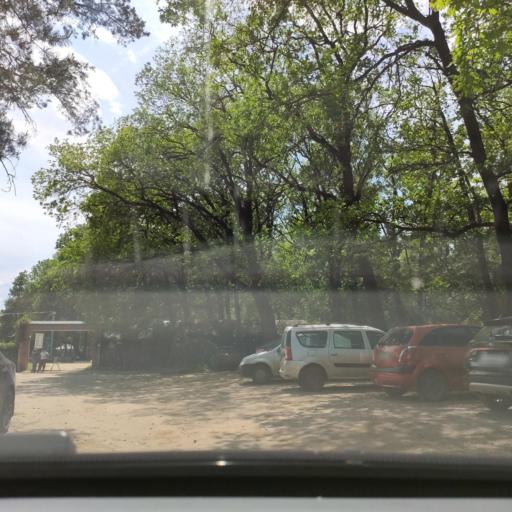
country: RU
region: Voronezj
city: Podgornoye
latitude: 51.8052
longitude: 39.1491
